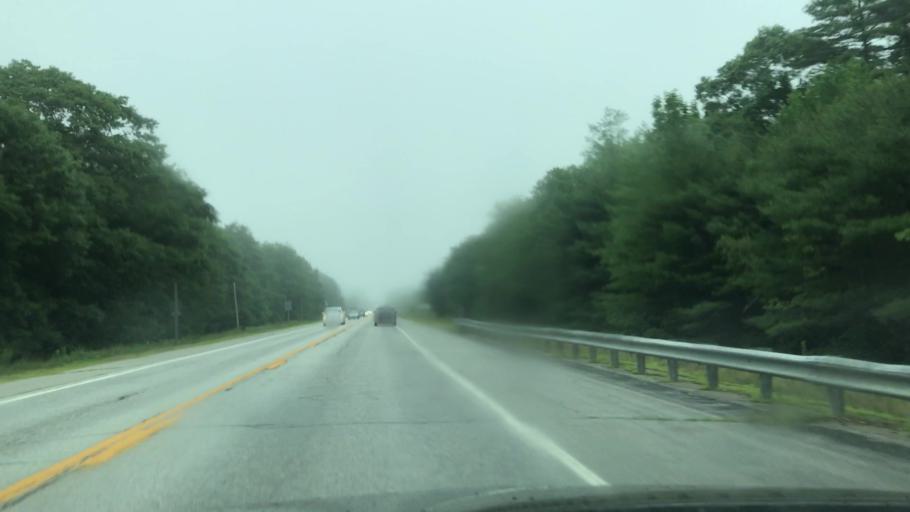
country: US
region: Maine
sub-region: Lincoln County
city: Nobleboro
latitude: 44.0614
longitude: -69.4941
